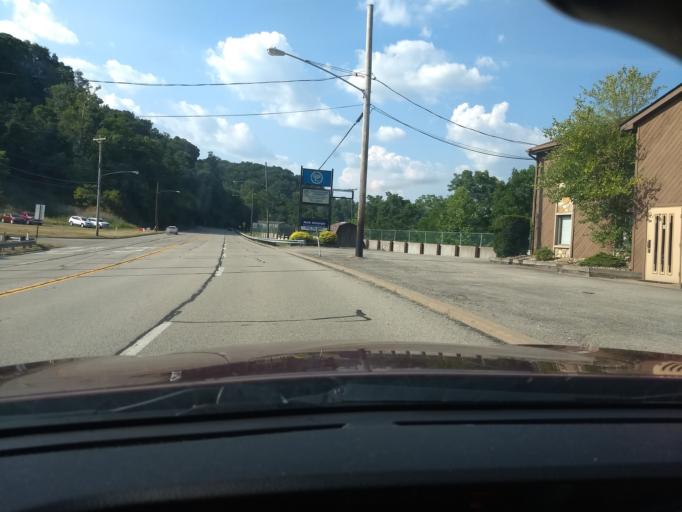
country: US
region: Pennsylvania
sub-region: Allegheny County
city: White Oak
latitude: 40.3248
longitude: -79.8180
